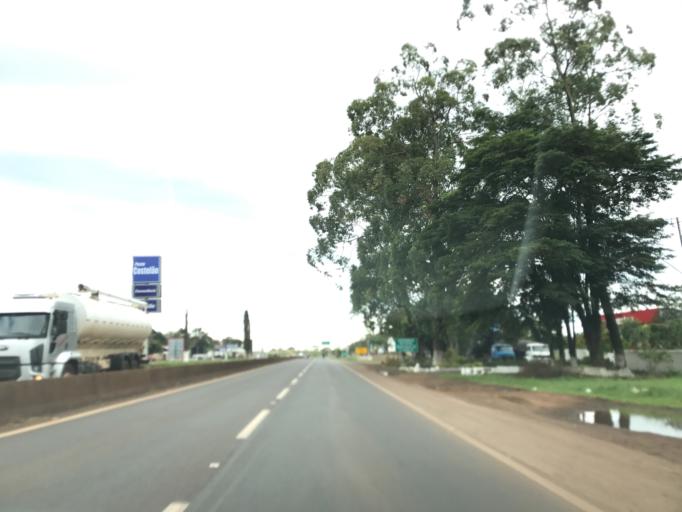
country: BR
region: Parana
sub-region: Rolandia
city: Rolandia
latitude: -23.3541
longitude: -51.3913
